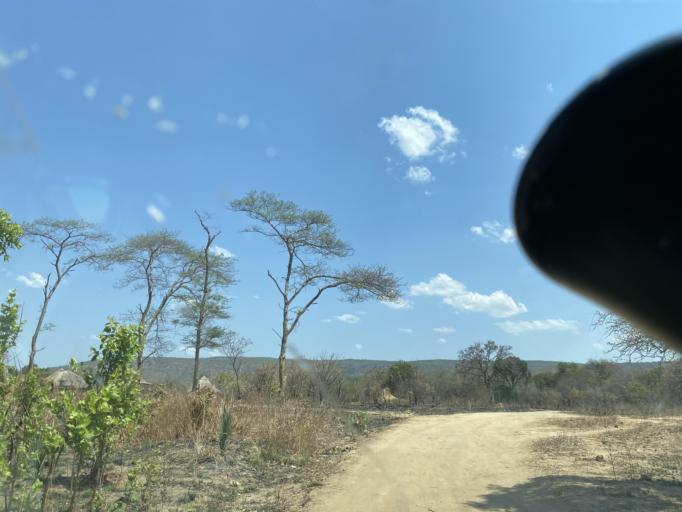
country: ZM
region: Lusaka
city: Chongwe
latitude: -15.0835
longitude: 29.4999
